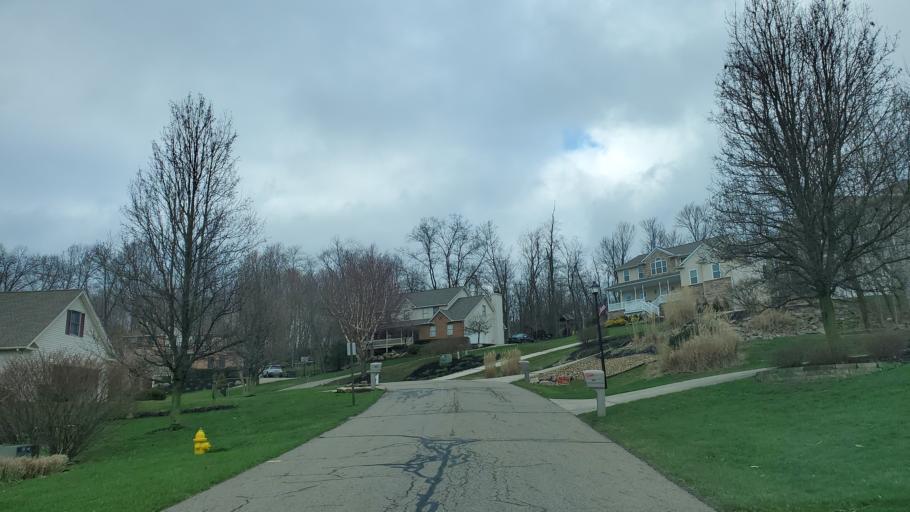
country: US
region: Ohio
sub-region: Licking County
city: Newark
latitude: 40.0351
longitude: -82.3759
